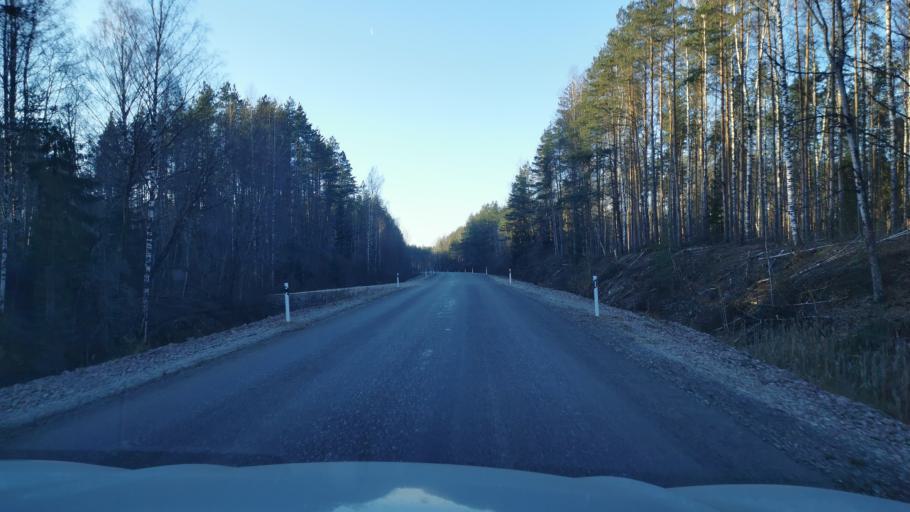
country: EE
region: Ida-Virumaa
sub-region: Kohtla-Nomme vald
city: Kohtla-Nomme
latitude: 59.3415
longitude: 27.1410
